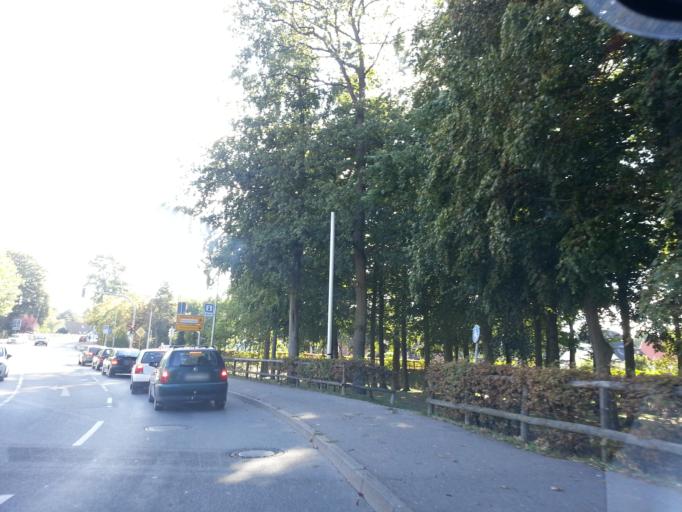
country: DE
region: Schleswig-Holstein
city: Heiligenhafen
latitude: 54.3719
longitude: 10.9732
